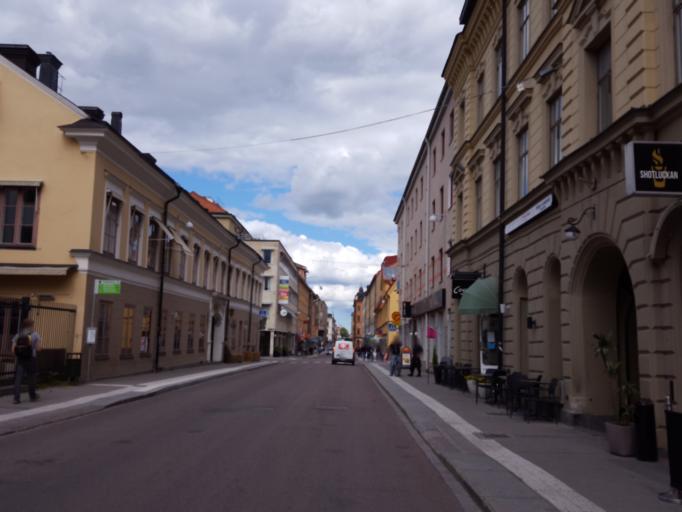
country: SE
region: Uppsala
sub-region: Uppsala Kommun
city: Uppsala
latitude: 59.8566
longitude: 17.6347
